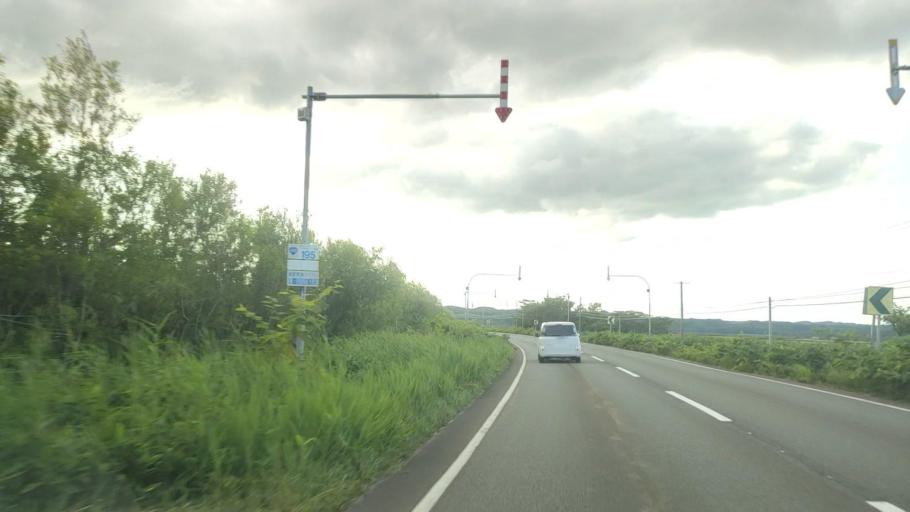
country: JP
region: Hokkaido
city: Makubetsu
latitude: 45.0042
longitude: 141.8131
